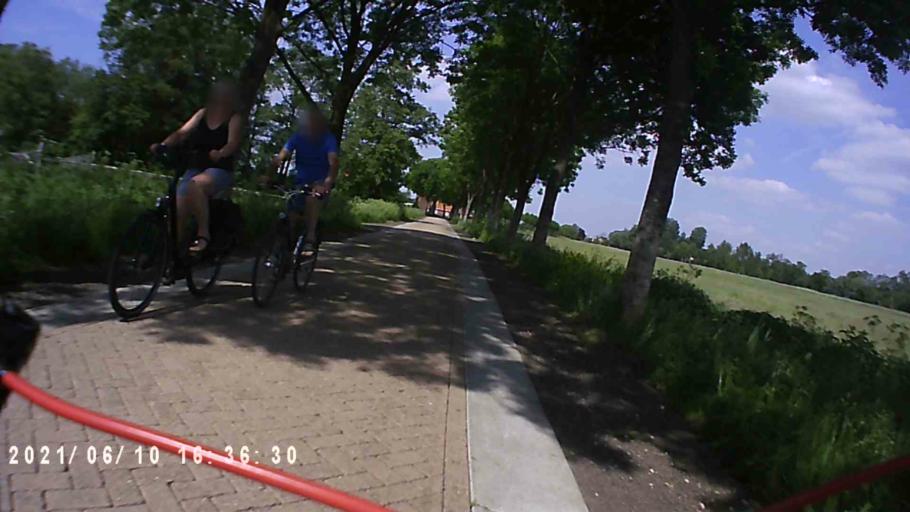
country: NL
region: Friesland
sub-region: Gemeente Achtkarspelen
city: Buitenpost
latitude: 53.2375
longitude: 6.1391
